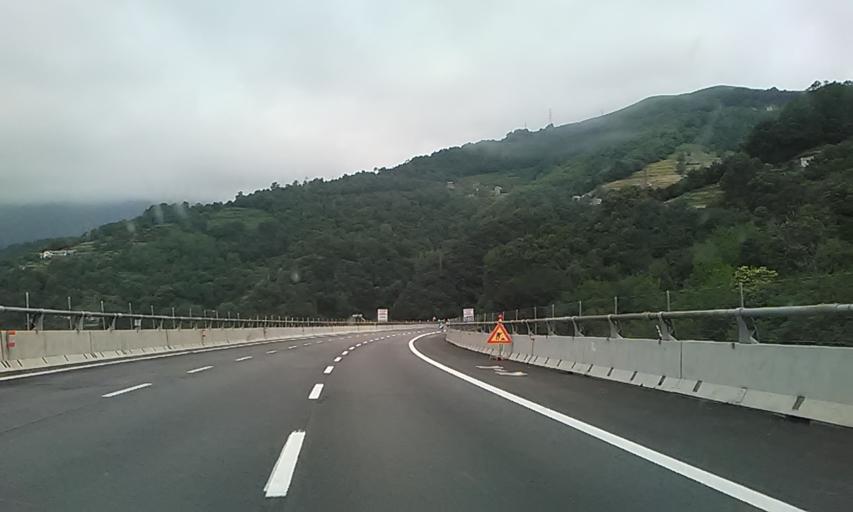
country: IT
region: Liguria
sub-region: Provincia di Genova
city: Mele
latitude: 44.4484
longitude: 8.7303
